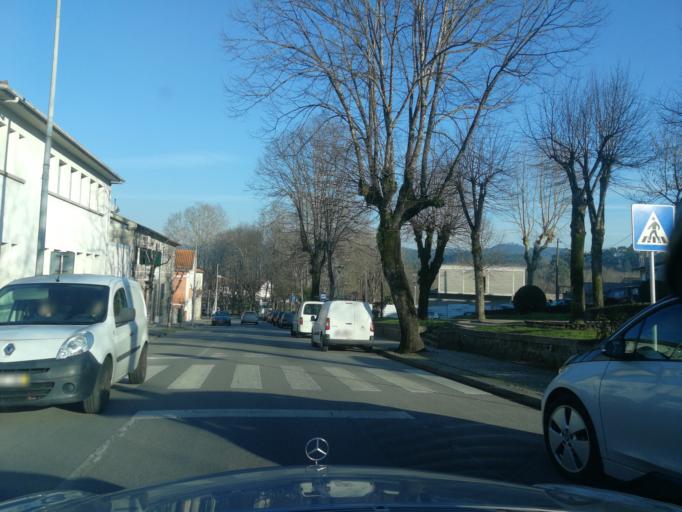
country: PT
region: Braga
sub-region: Guimaraes
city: Ponte
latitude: 41.4861
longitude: -8.3441
